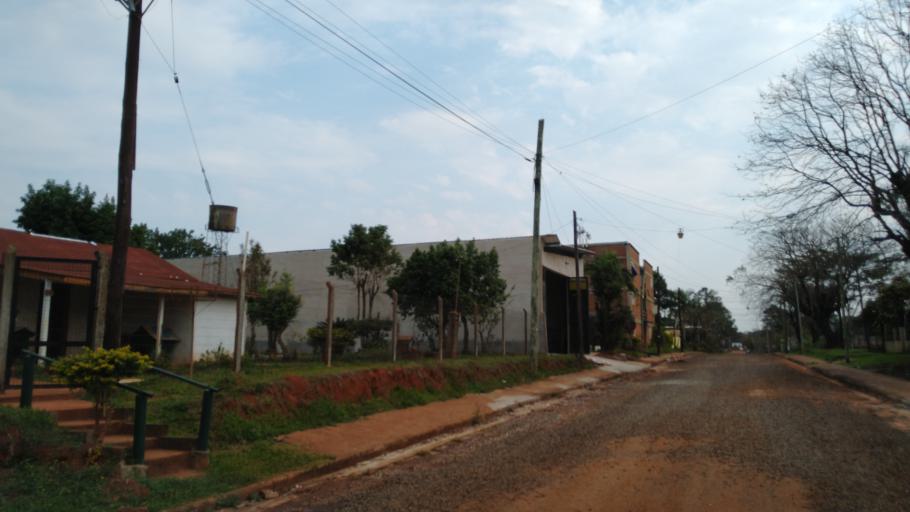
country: AR
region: Misiones
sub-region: Departamento de Capital
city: Posadas
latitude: -27.4334
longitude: -55.8806
